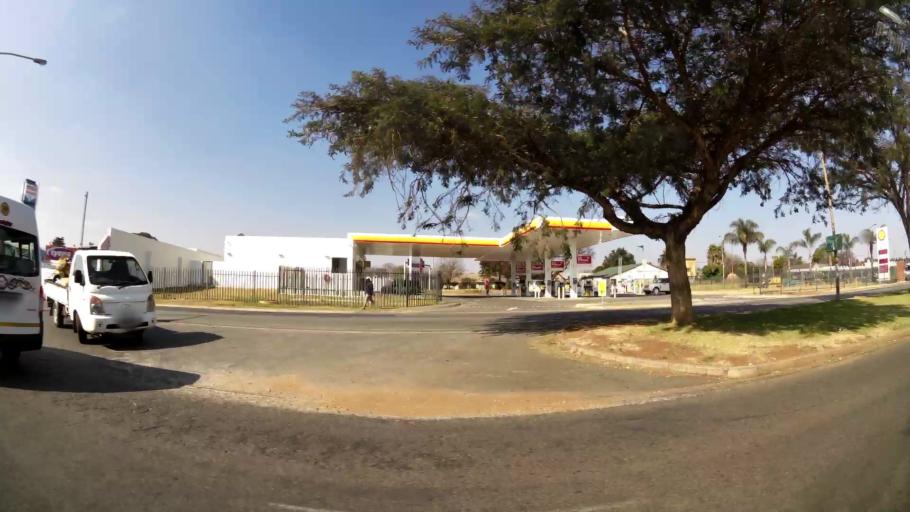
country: ZA
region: Gauteng
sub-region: City of Johannesburg Metropolitan Municipality
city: Modderfontein
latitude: -26.1143
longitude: 28.2288
